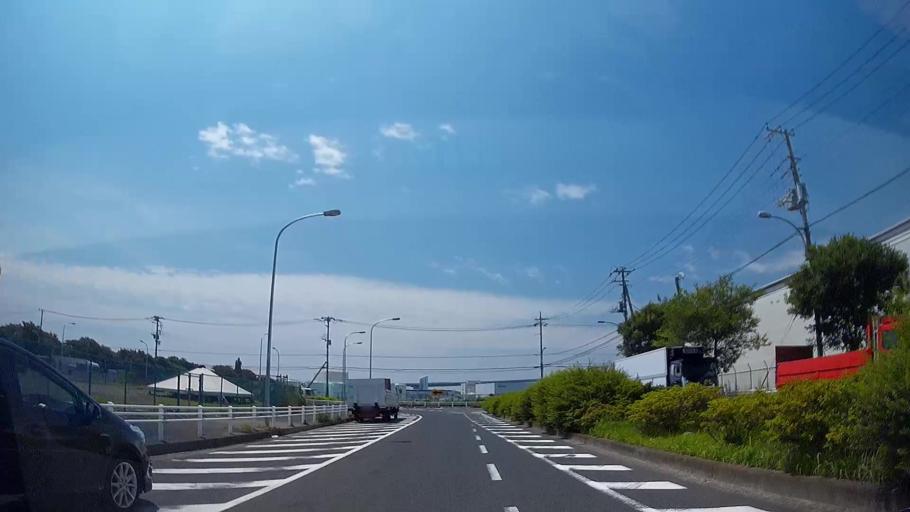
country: JP
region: Tokyo
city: Urayasu
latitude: 35.6232
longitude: 139.8316
